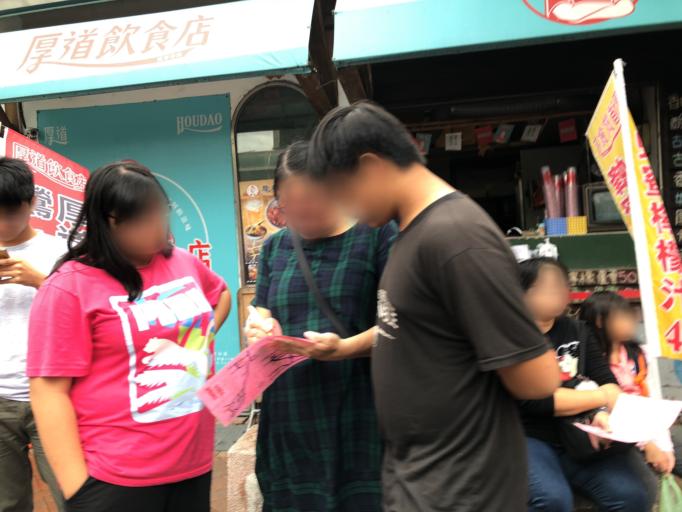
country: TW
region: Taiwan
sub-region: Taoyuan
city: Taoyuan
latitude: 24.9516
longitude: 121.3474
